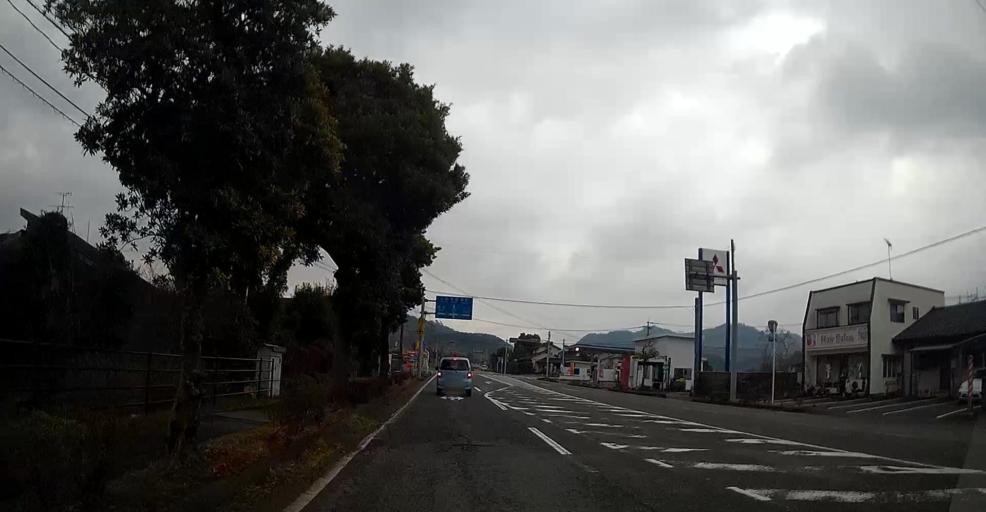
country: JP
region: Kumamoto
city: Matsubase
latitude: 32.6494
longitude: 130.7149
